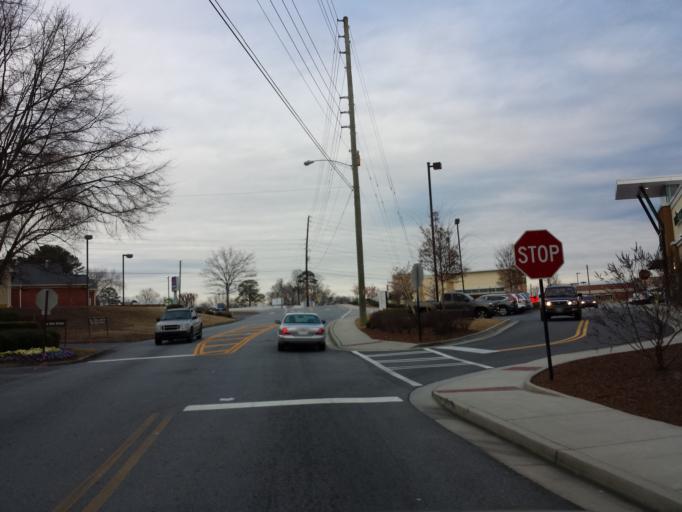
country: US
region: Georgia
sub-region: Fulton County
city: Sandy Springs
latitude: 33.9814
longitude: -84.4279
